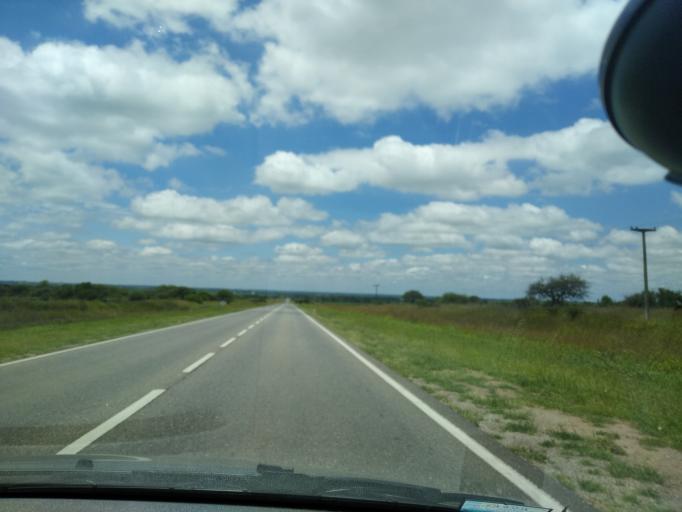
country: AR
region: Cordoba
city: Alta Gracia
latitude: -31.6521
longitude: -64.3075
